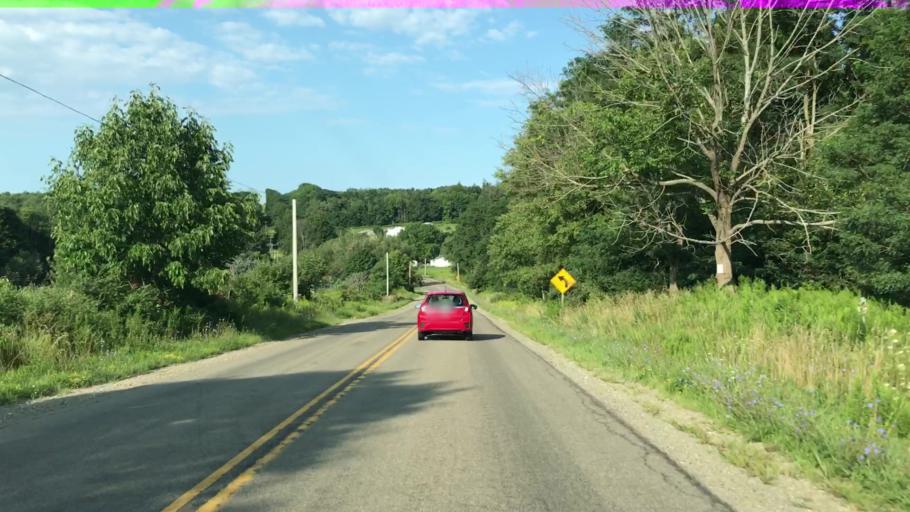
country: US
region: New York
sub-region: Chautauqua County
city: Mayville
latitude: 42.2858
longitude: -79.4320
